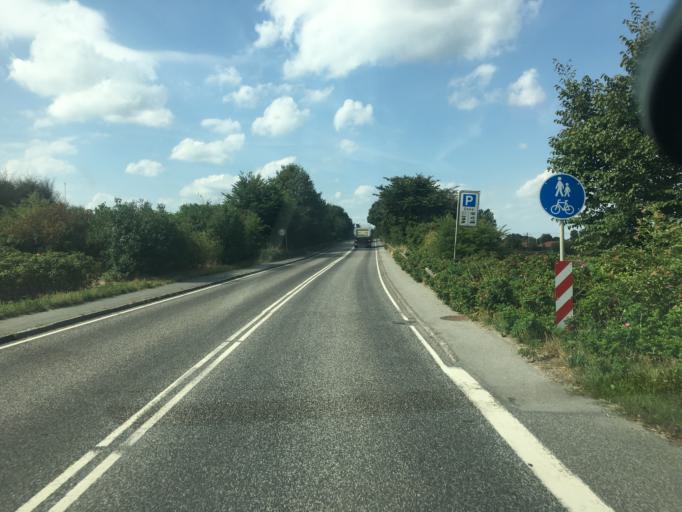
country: DK
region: South Denmark
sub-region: Aabenraa Kommune
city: Tinglev
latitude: 54.9407
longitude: 9.2635
